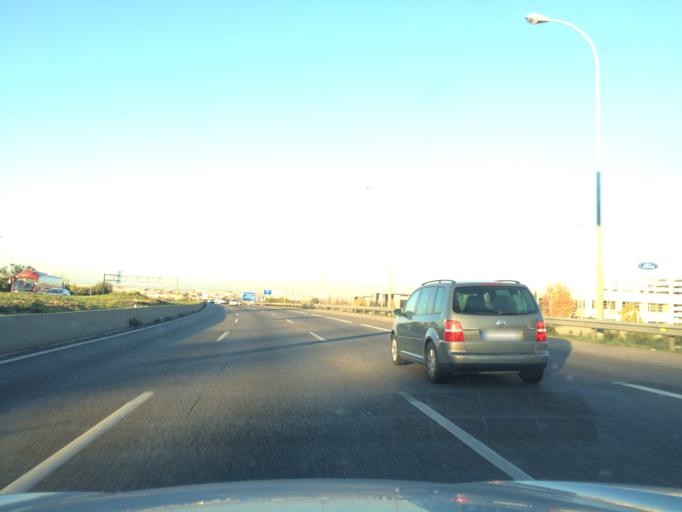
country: ES
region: Madrid
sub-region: Provincia de Madrid
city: Alcobendas
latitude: 40.5247
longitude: -3.6492
